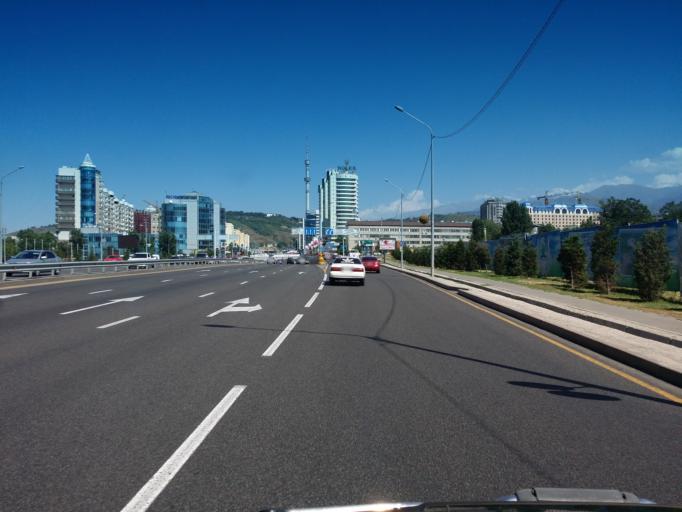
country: KZ
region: Almaty Qalasy
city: Almaty
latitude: 43.2278
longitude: 76.9462
